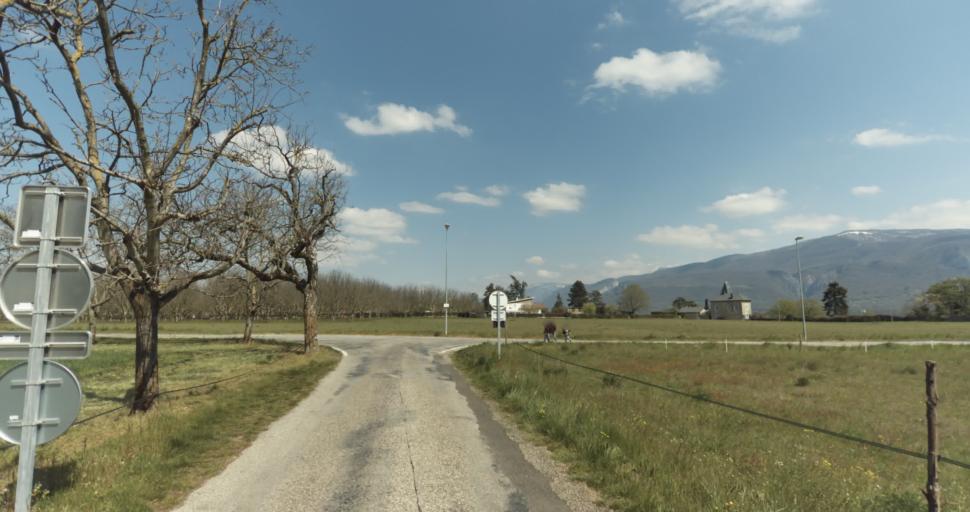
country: FR
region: Rhone-Alpes
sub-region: Departement de l'Isere
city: Saint-Marcellin
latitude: 45.1395
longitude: 5.3217
